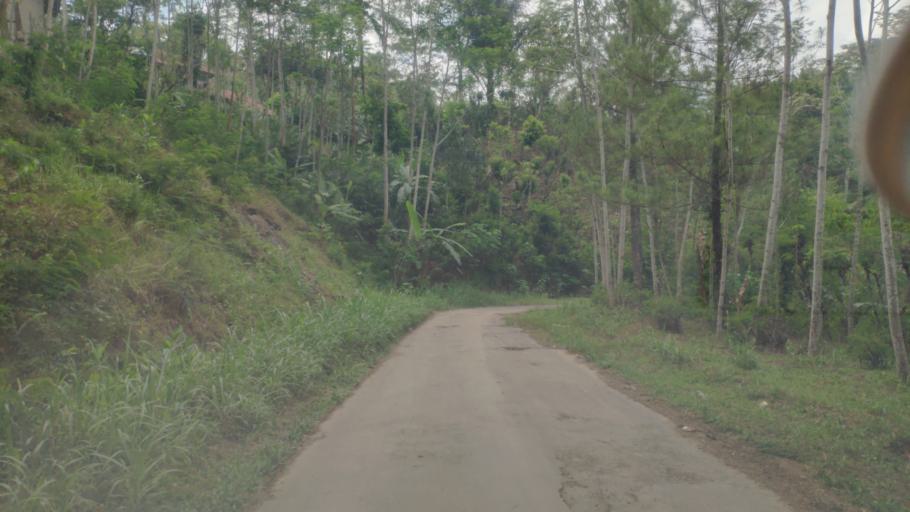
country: ID
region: Central Java
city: Wonosobo
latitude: -7.3194
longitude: 109.7847
